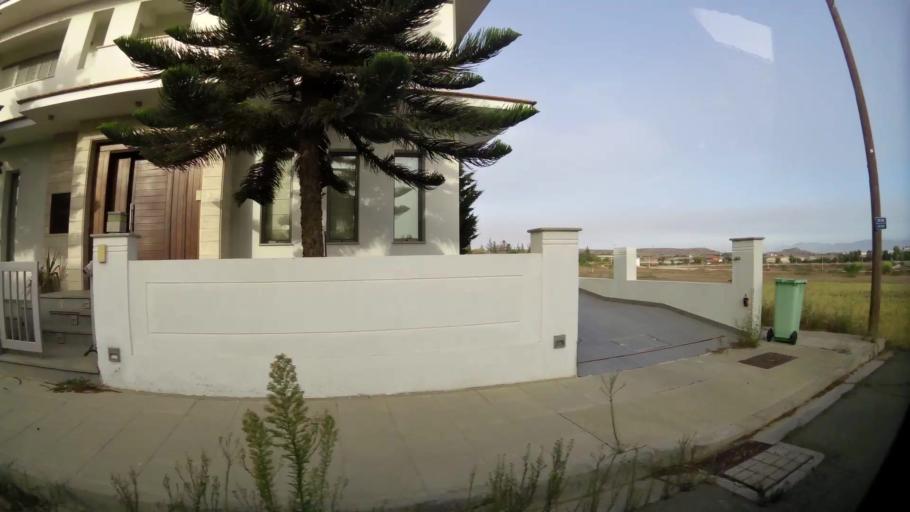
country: CY
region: Lefkosia
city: Geri
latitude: 35.0690
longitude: 33.3807
